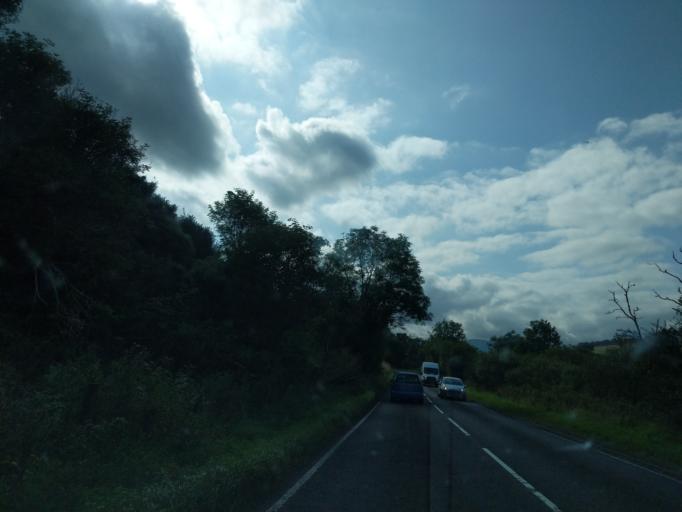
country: GB
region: Scotland
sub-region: The Scottish Borders
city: Peebles
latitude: 55.6792
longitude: -3.2060
